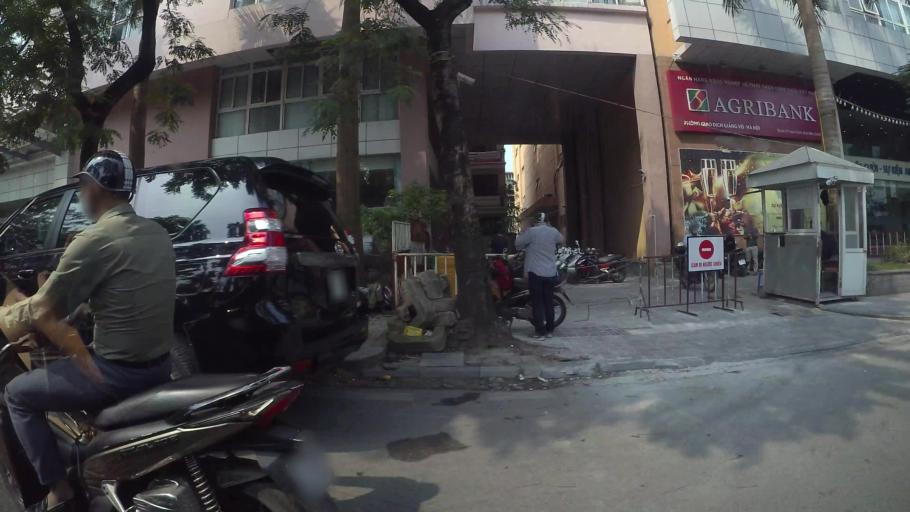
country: VN
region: Ha Noi
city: Dong Da
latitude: 21.0245
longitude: 105.8196
